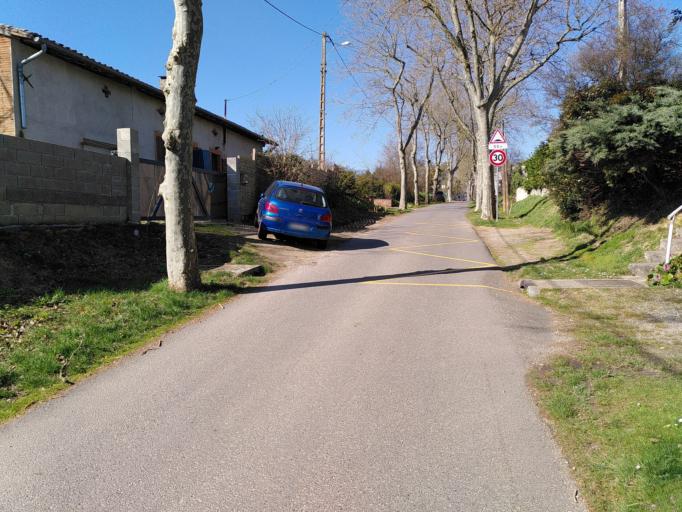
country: FR
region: Midi-Pyrenees
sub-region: Departement de la Haute-Garonne
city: Pompertuzat
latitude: 43.4519
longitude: 1.4934
